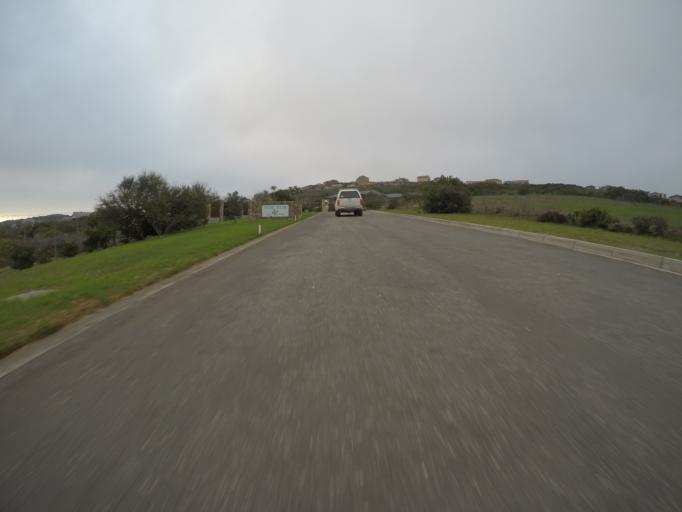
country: ZA
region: Western Cape
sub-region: Eden District Municipality
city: Mossel Bay
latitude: -34.1418
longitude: 22.0894
